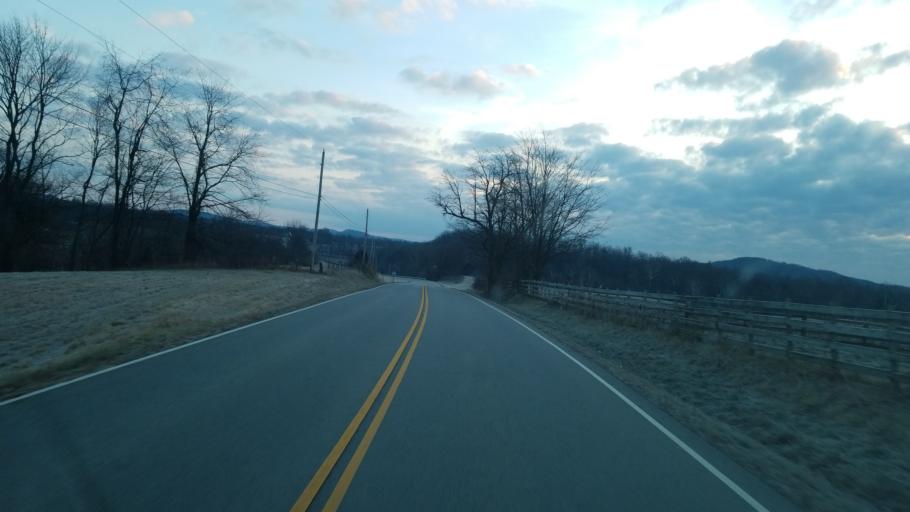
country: US
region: Ohio
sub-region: Highland County
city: Greenfield
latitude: 39.2214
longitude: -83.4049
